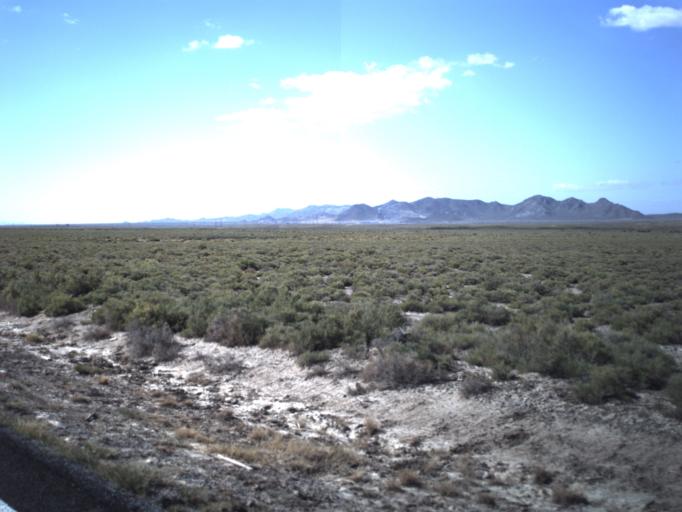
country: US
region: Utah
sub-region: Beaver County
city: Milford
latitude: 38.5258
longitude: -112.9912
